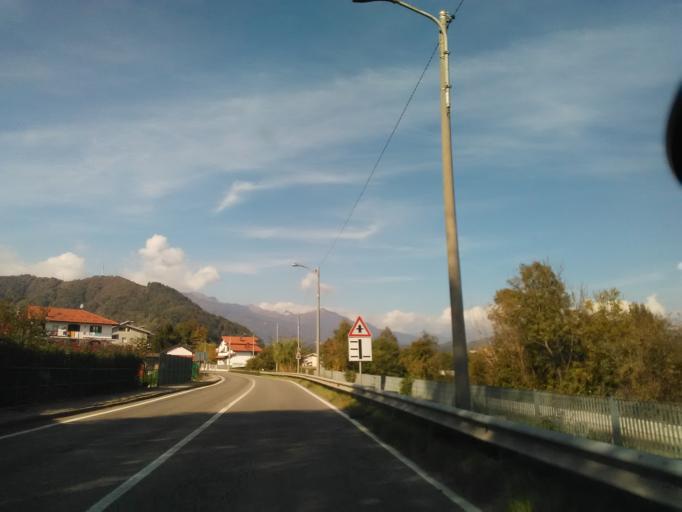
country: IT
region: Piedmont
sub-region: Provincia di Vercelli
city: Serravalle Sesia
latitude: 45.6948
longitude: 8.2975
